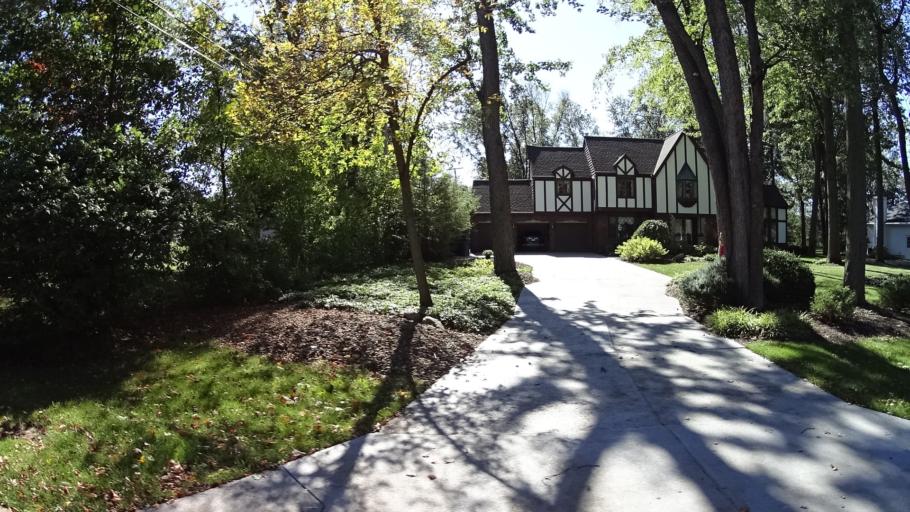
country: US
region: Ohio
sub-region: Lorain County
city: Amherst
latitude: 41.4075
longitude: -82.2176
